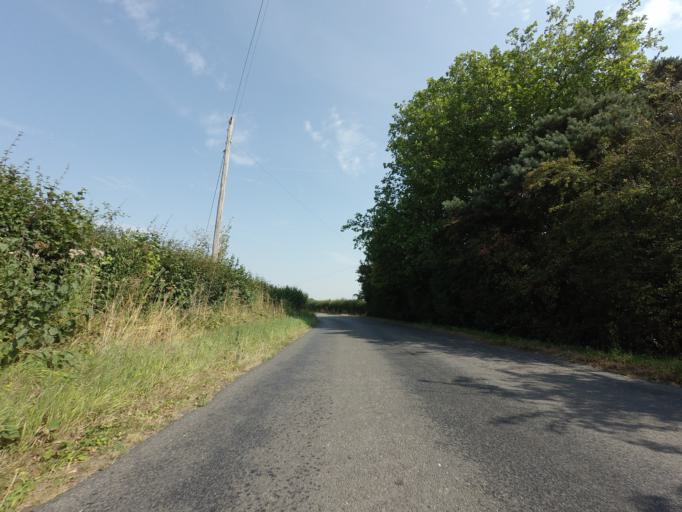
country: GB
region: England
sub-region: Kent
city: Headcorn
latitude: 51.1585
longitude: 0.6066
